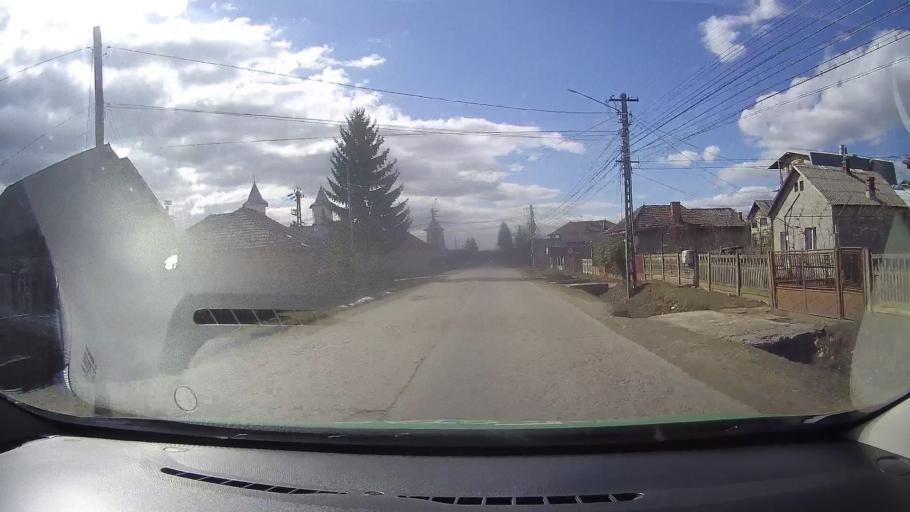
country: RO
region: Dambovita
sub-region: Comuna Branesti
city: Branesti
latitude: 45.0340
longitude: 25.4138
